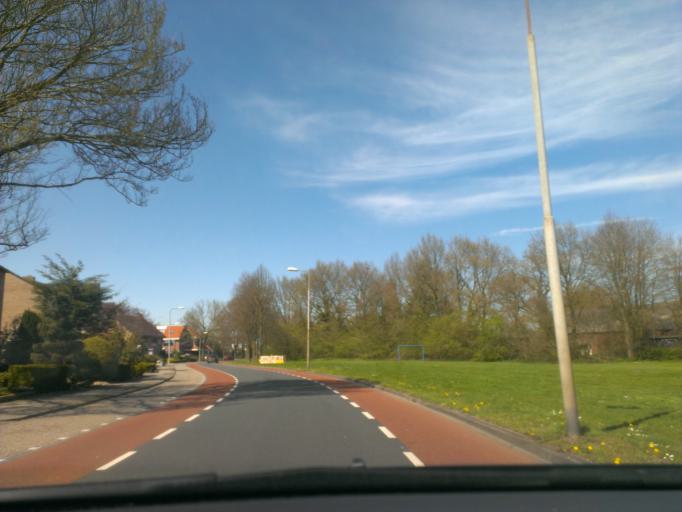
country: NL
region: Overijssel
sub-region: Gemeente Twenterand
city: Den Ham
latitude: 52.3922
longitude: 6.4560
